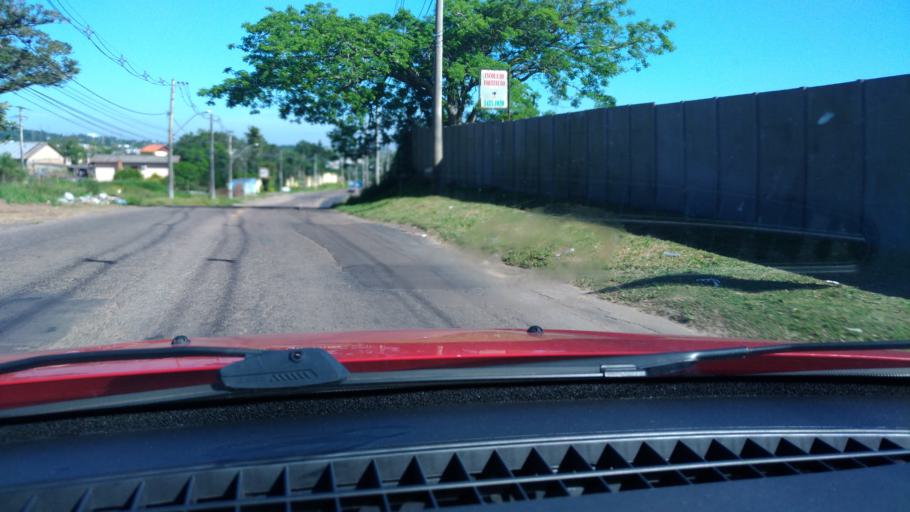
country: BR
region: Rio Grande do Sul
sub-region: Viamao
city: Viamao
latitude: -30.0474
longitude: -51.0800
